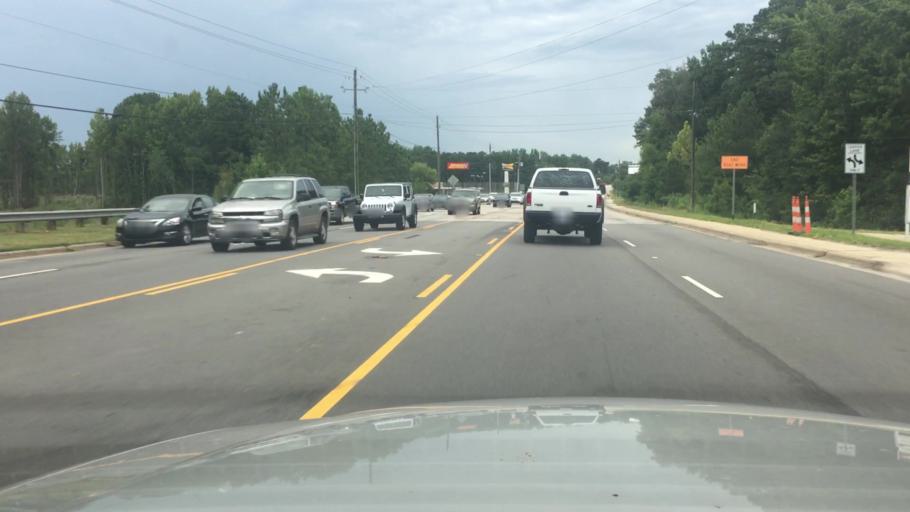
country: US
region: North Carolina
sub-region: Cumberland County
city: Hope Mills
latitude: 34.9877
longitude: -78.9657
